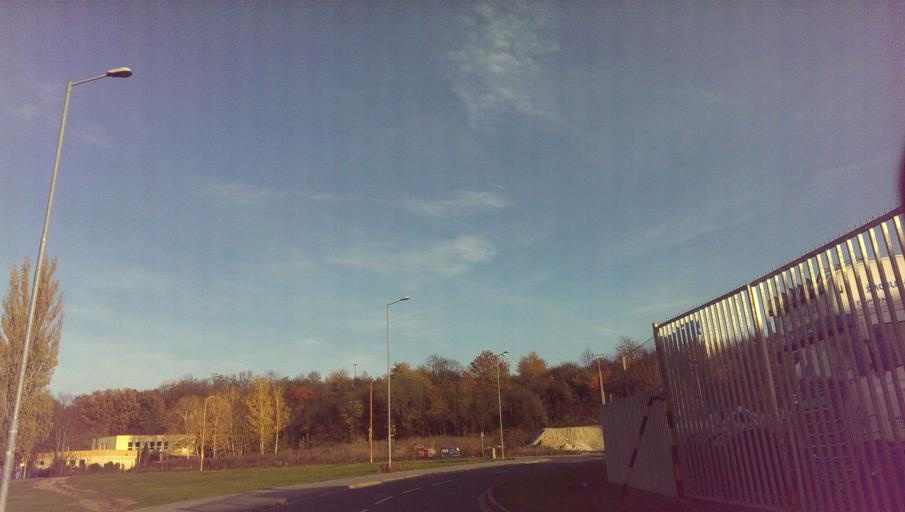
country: CZ
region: Zlin
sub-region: Okres Uherske Hradiste
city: Uherske Hradiste
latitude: 49.0622
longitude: 17.4687
